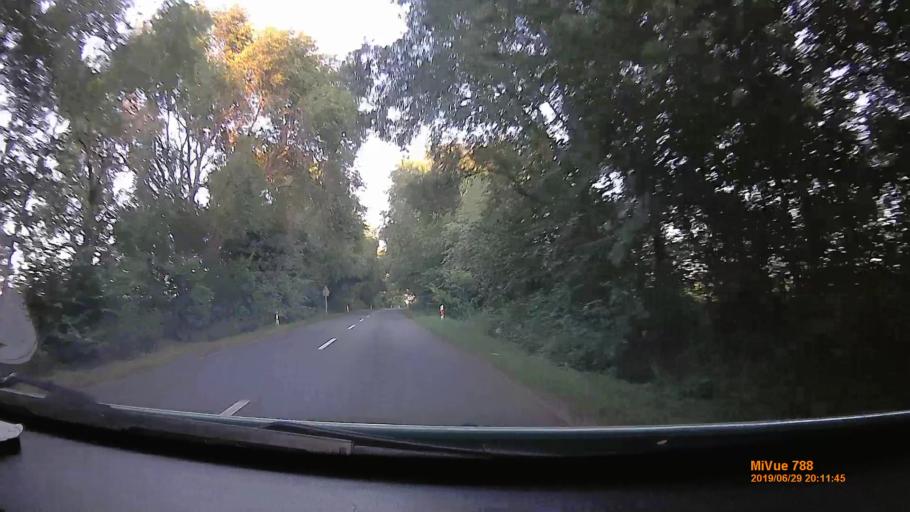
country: HU
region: Pest
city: Paty
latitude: 47.5246
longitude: 18.7969
